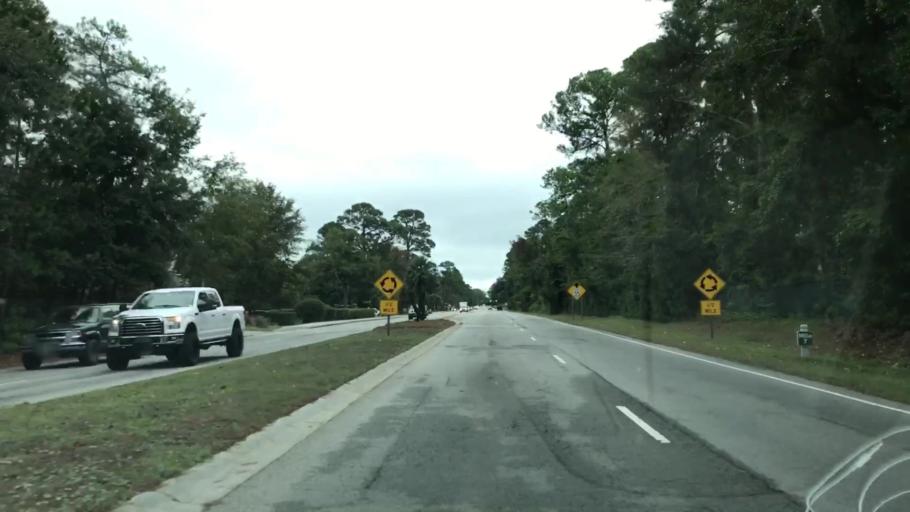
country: US
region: South Carolina
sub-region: Beaufort County
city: Hilton Head Island
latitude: 32.1631
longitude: -80.7691
